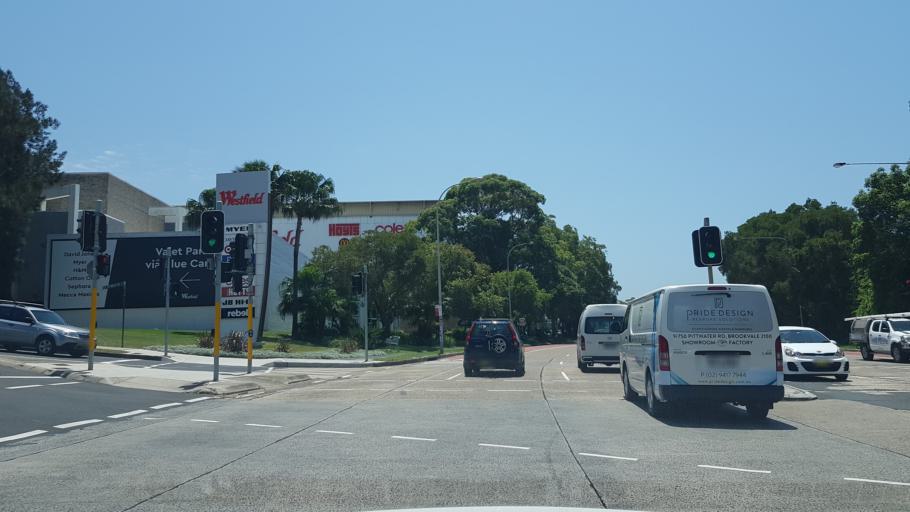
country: AU
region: New South Wales
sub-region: Warringah
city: North Manly
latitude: -33.7704
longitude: 151.2659
